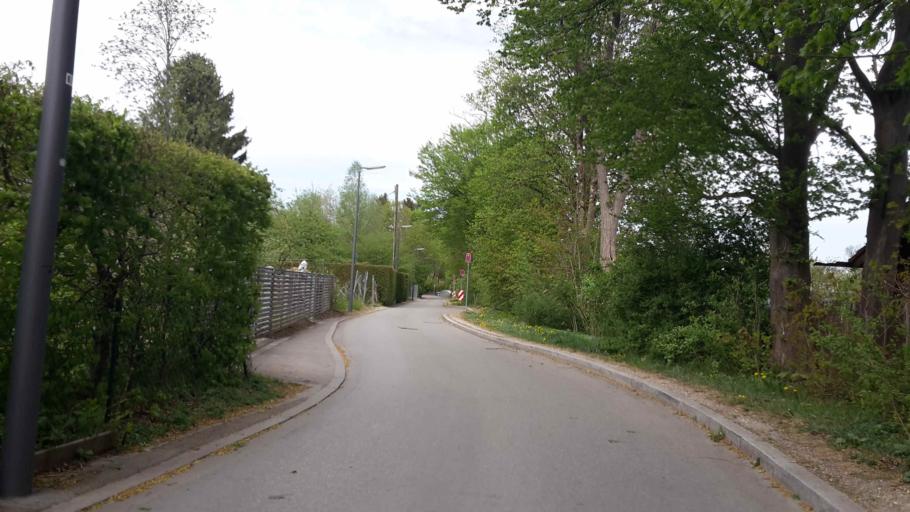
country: DE
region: Bavaria
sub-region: Upper Bavaria
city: Karlsfeld
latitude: 48.1847
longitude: 11.4901
